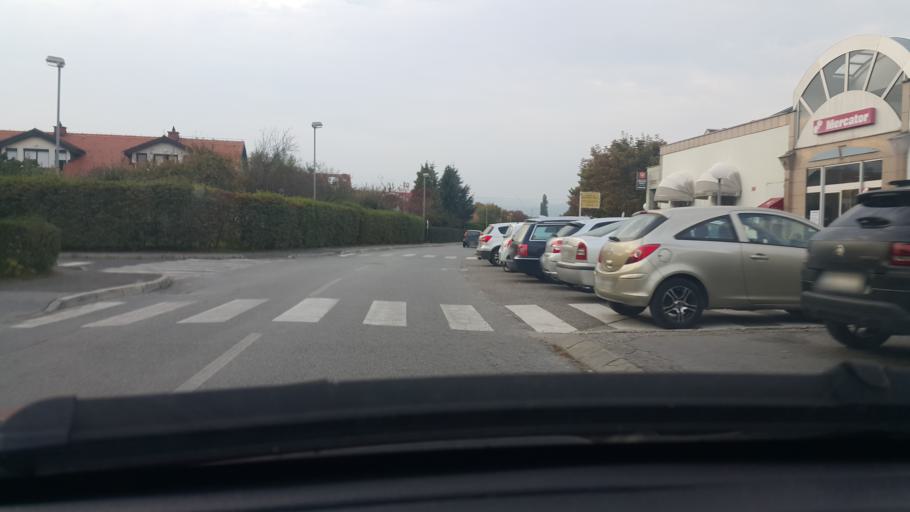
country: SI
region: Maribor
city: Razvanje
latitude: 46.5368
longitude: 15.6241
